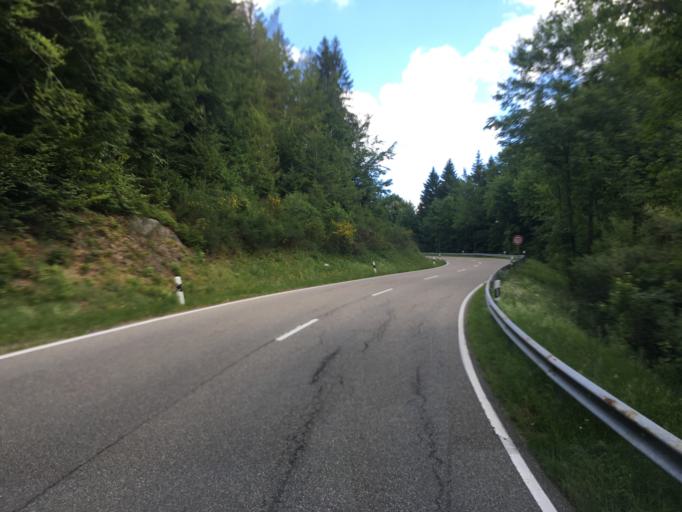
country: DE
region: Baden-Wuerttemberg
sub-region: Karlsruhe Region
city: Forbach
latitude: 48.6503
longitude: 8.3310
